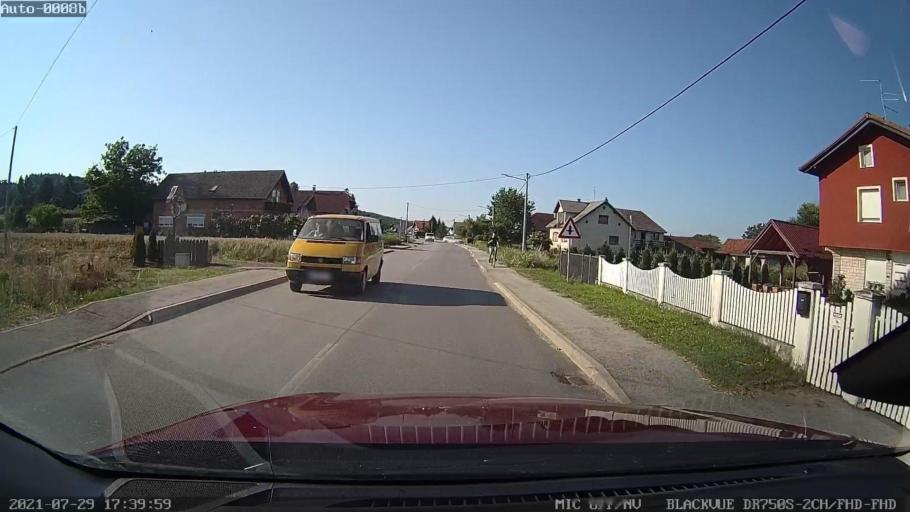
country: HR
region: Varazdinska
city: Vinica
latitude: 46.3192
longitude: 16.1564
